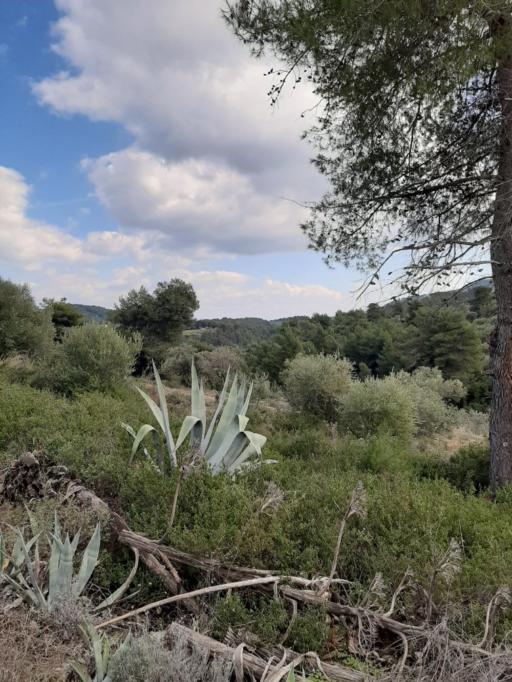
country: GR
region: Attica
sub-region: Nomarchia Anatolikis Attikis
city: Markopoulo Oropou
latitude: 38.2947
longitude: 23.8244
